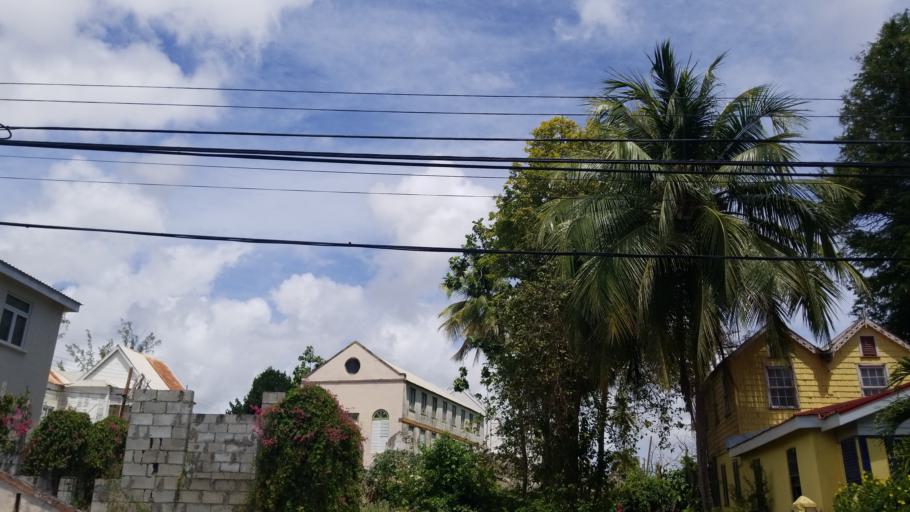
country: BB
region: Saint Michael
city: Bridgetown
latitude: 13.0898
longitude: -59.6088
